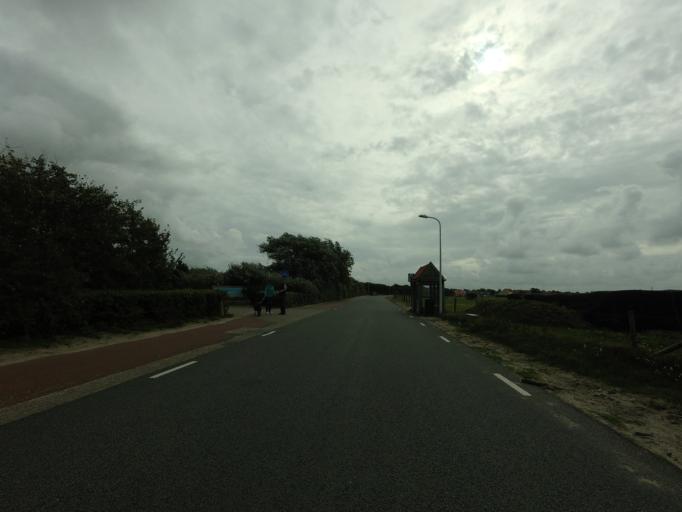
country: NL
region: Friesland
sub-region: Gemeente Ameland
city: Hollum
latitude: 53.4474
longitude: 5.6325
